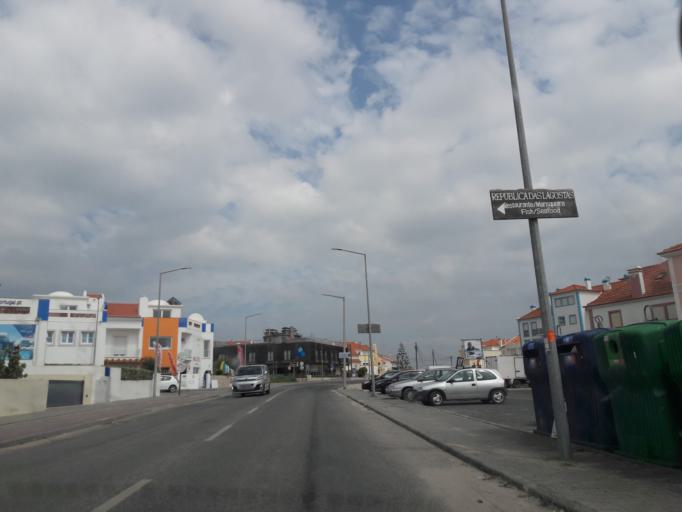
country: PT
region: Leiria
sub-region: Peniche
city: Atouguia da Baleia
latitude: 39.3709
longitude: -9.3298
